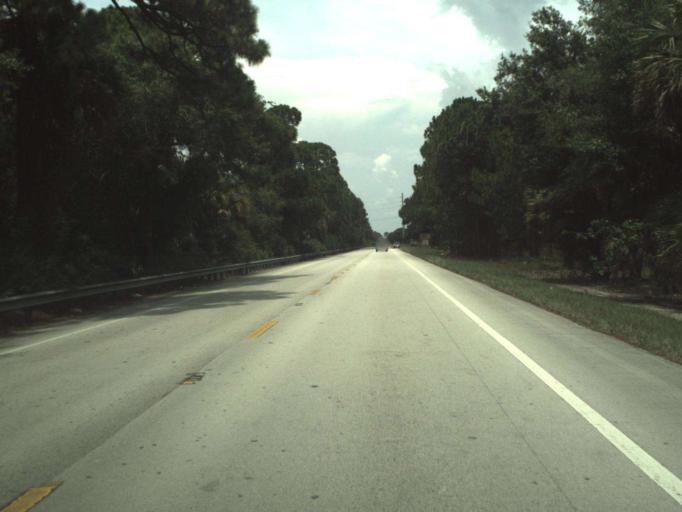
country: US
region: Florida
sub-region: Saint Lucie County
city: Lakewood Park
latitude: 27.5107
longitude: -80.3984
